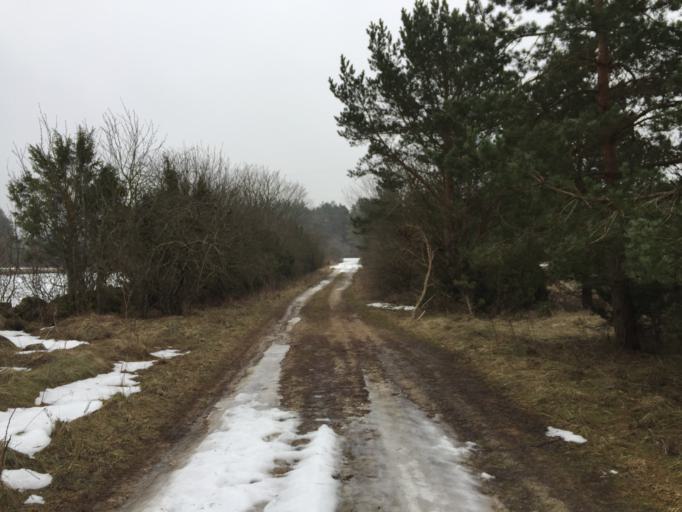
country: EE
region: Saare
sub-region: Orissaare vald
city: Orissaare
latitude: 58.4175
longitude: 22.8224
